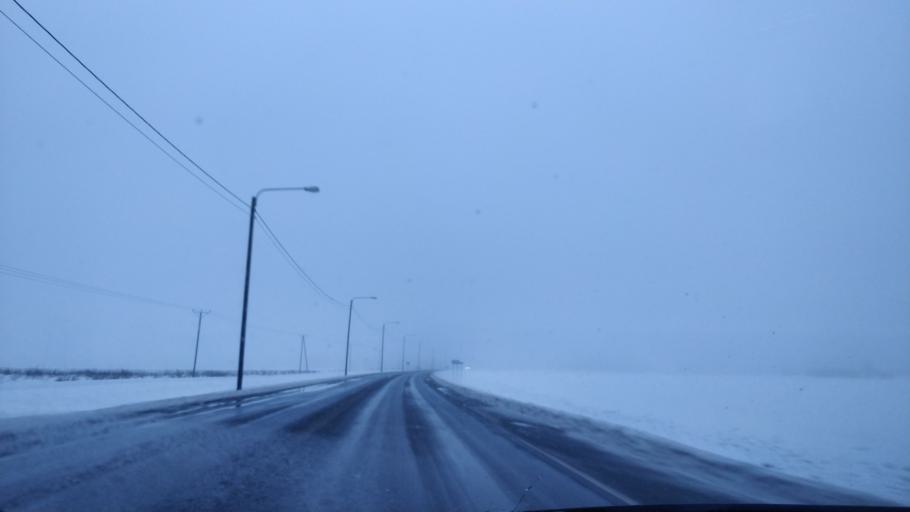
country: FI
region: Lapland
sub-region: Kemi-Tornio
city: Tervola
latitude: 66.1510
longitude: 24.9830
